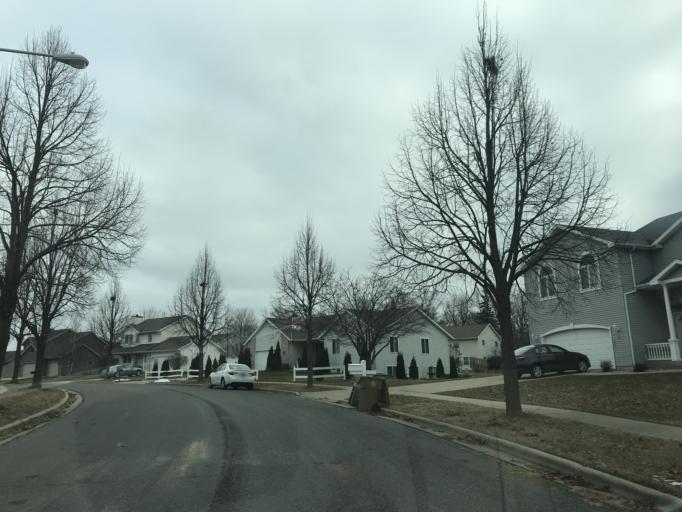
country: US
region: Wisconsin
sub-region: Dane County
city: Monona
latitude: 43.1074
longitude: -89.2928
